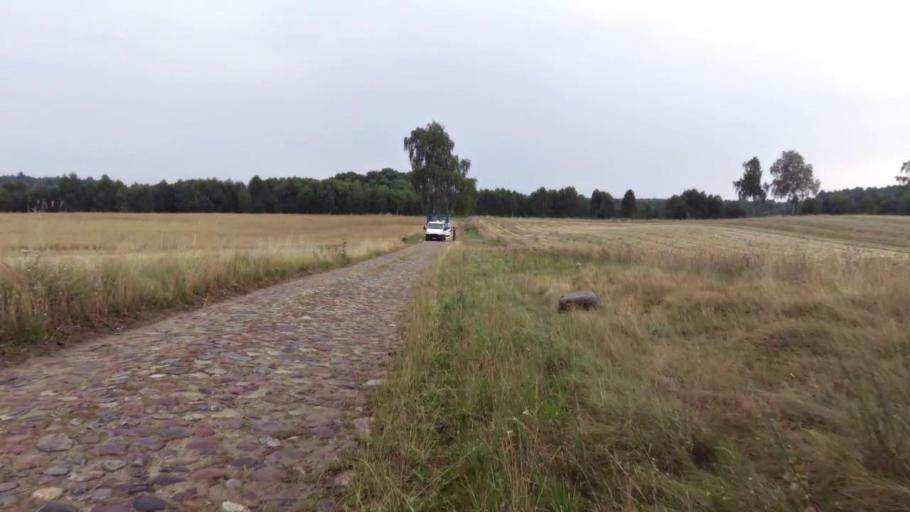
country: PL
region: West Pomeranian Voivodeship
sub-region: Powiat szczecinecki
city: Lubowo
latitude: 53.6107
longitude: 16.3516
